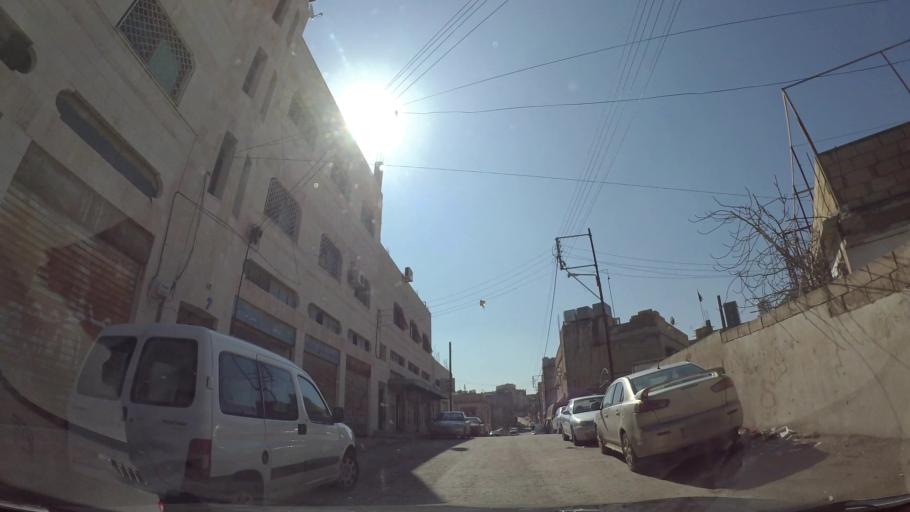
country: JO
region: Amman
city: Amman
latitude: 31.9898
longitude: 35.9851
